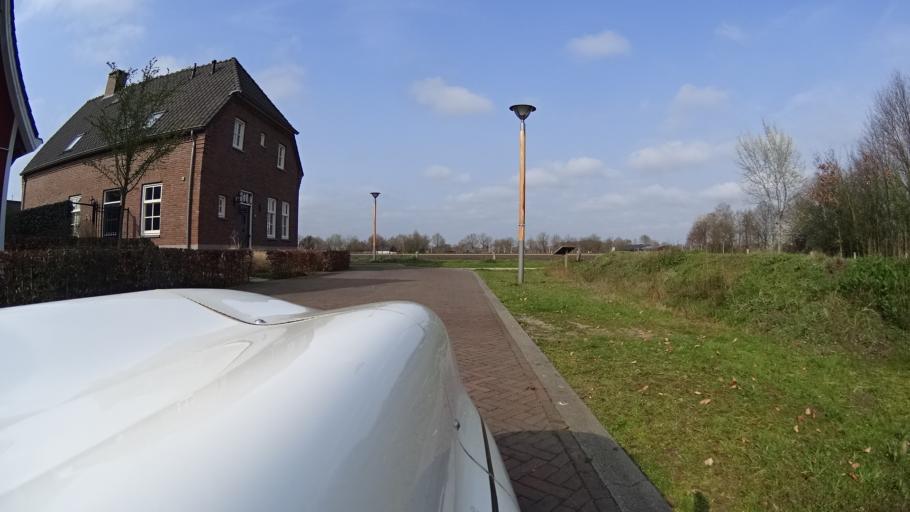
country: NL
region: North Brabant
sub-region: Gemeente Boekel
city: Boekel
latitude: 51.5699
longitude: 5.6931
